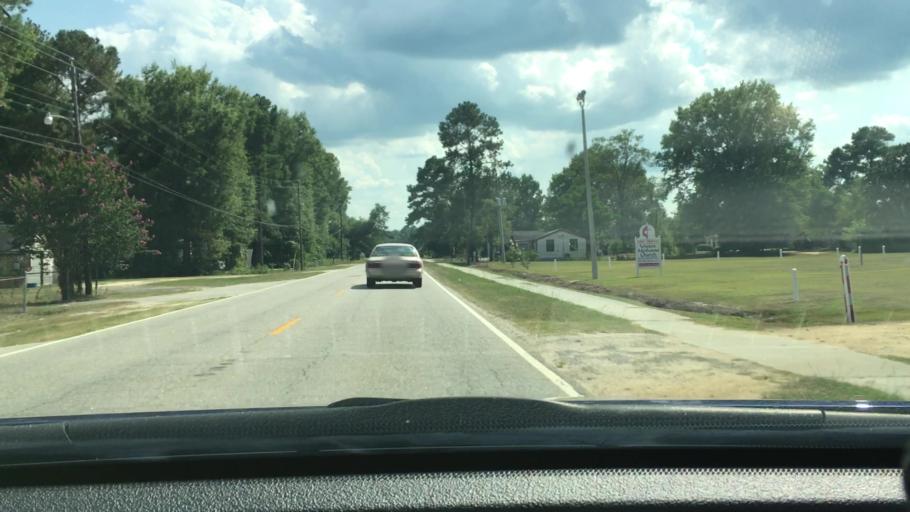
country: US
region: South Carolina
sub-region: Florence County
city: Timmonsville
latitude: 34.1654
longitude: -80.0665
